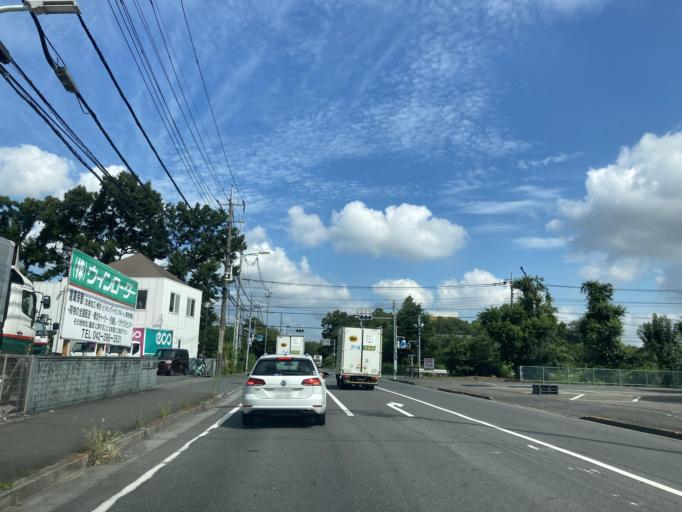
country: JP
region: Tokyo
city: Higashimurayama-shi
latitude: 35.7578
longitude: 139.4949
